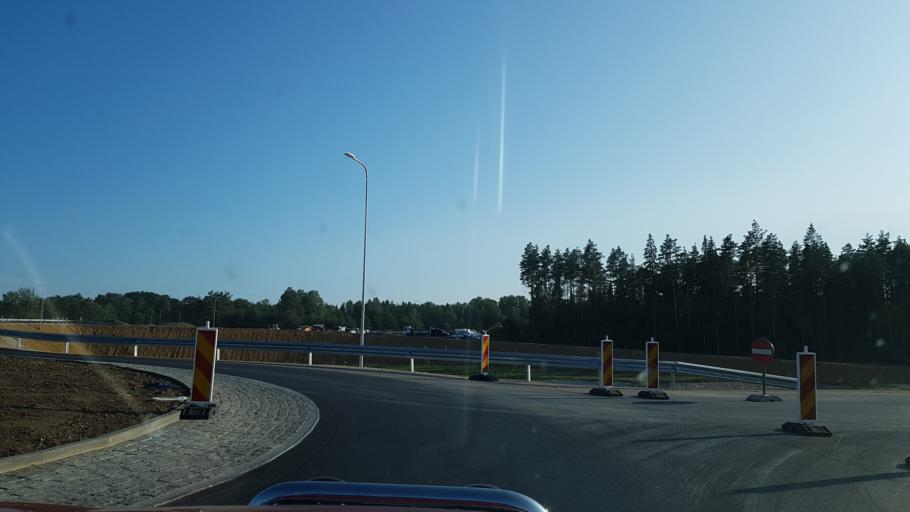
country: EE
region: Harju
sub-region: Raasiku vald
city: Raasiku
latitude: 59.1597
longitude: 25.1896
